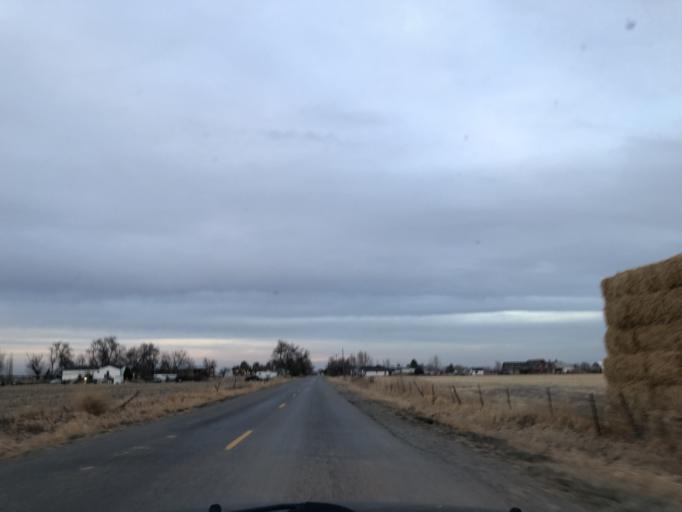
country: US
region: Utah
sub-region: Cache County
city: Benson
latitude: 41.7839
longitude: -111.9118
